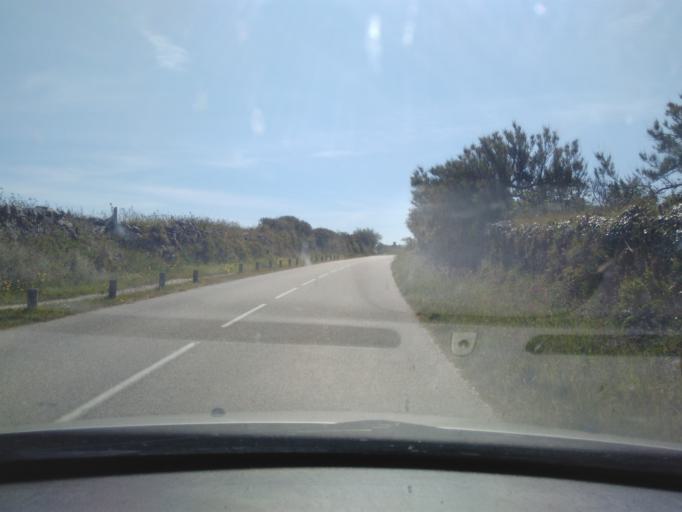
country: FR
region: Lower Normandy
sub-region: Departement de la Manche
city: Beaumont-Hague
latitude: 49.7151
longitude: -1.9367
